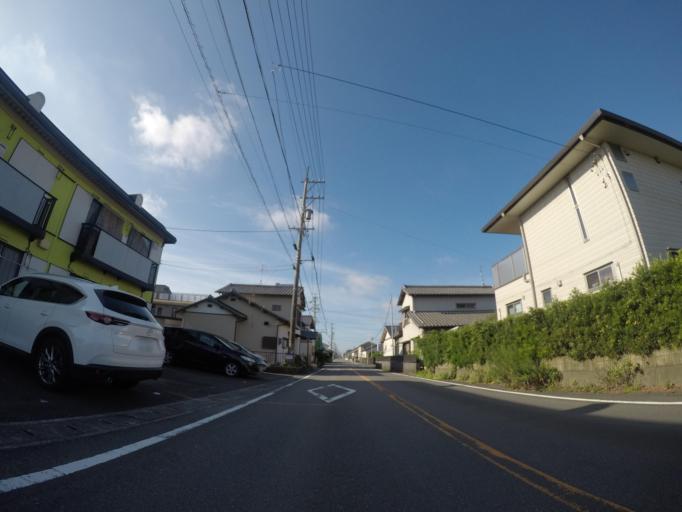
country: JP
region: Shizuoka
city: Yaizu
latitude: 34.8308
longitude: 138.3106
